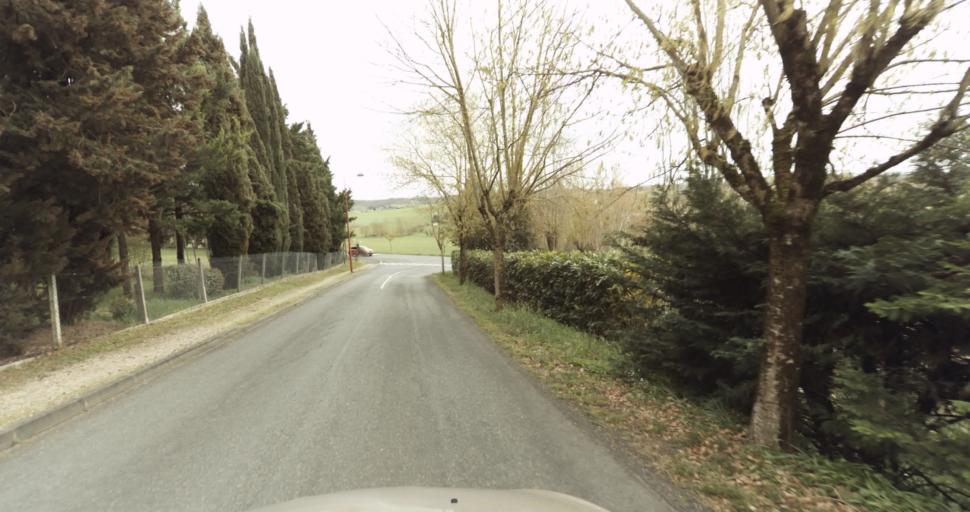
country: FR
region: Midi-Pyrenees
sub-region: Departement du Tarn
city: Puygouzon
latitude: 43.8928
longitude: 2.1720
